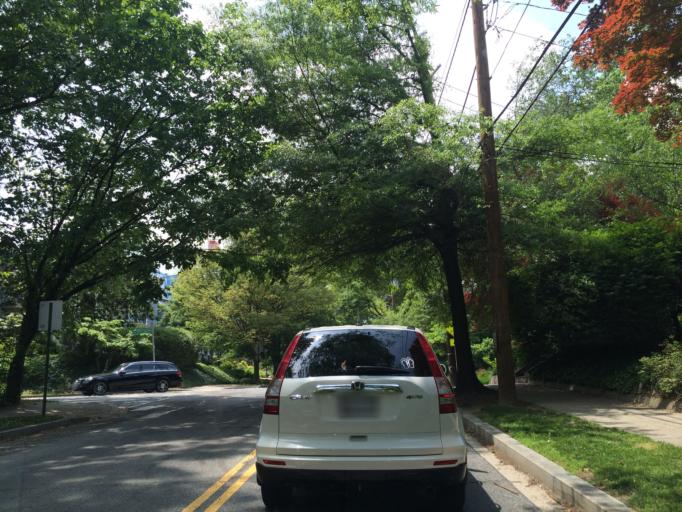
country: US
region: Maryland
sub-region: Montgomery County
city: Chevy Chase
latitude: 38.9611
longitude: -77.0705
